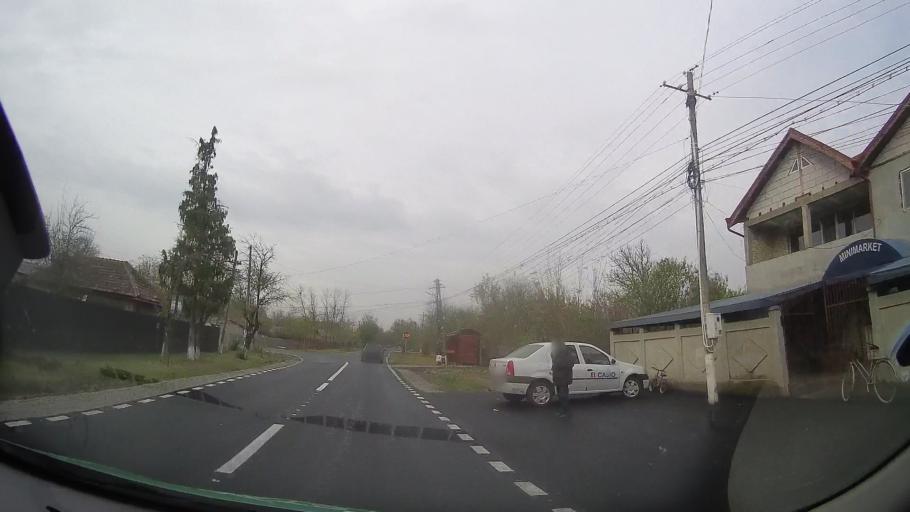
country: RO
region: Ilfov
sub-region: Comuna Nuci
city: Nuci
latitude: 44.7205
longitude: 26.3039
